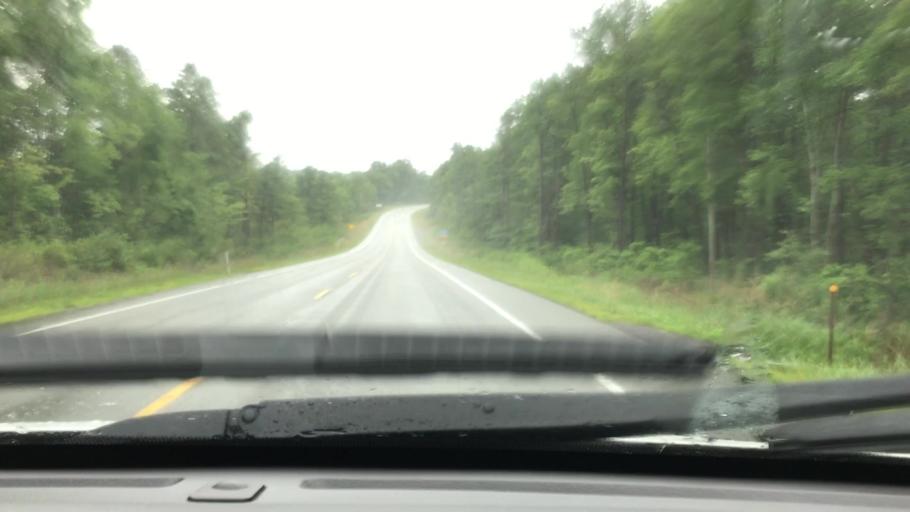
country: US
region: Pennsylvania
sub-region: Clearfield County
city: Osceola Mills
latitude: 40.8278
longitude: -78.2249
